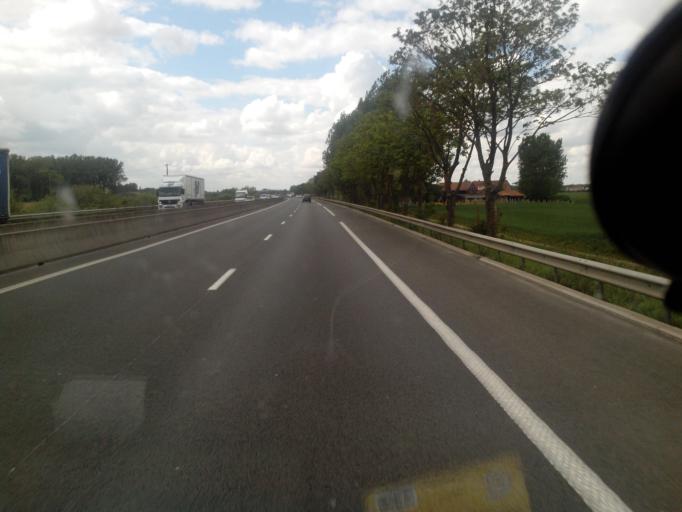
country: FR
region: Nord-Pas-de-Calais
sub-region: Departement du Nord
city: Steenwerck
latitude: 50.7112
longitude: 2.7757
